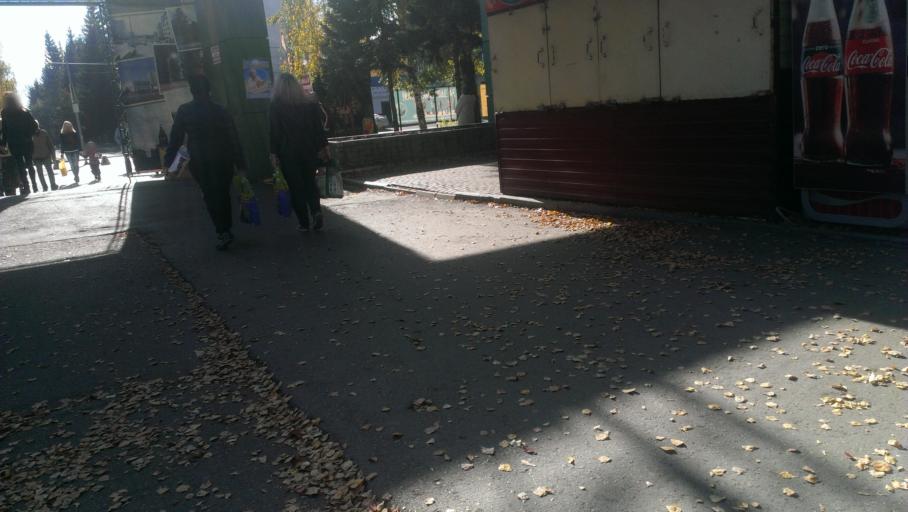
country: RU
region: Altai Krai
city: Novosilikatnyy
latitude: 53.3553
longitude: 83.6843
